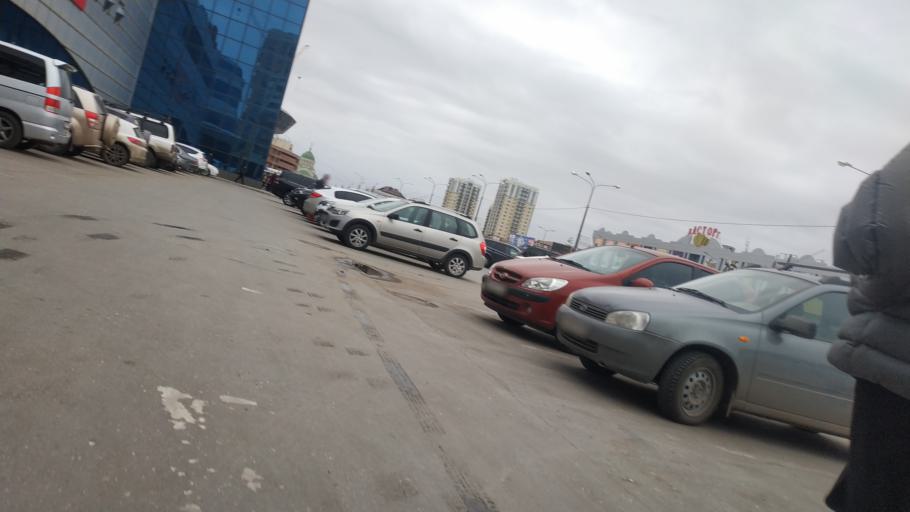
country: RU
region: Astrakhan
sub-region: Gorod Astrakhan'
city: Astrakhan'
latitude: 46.3395
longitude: 48.0248
